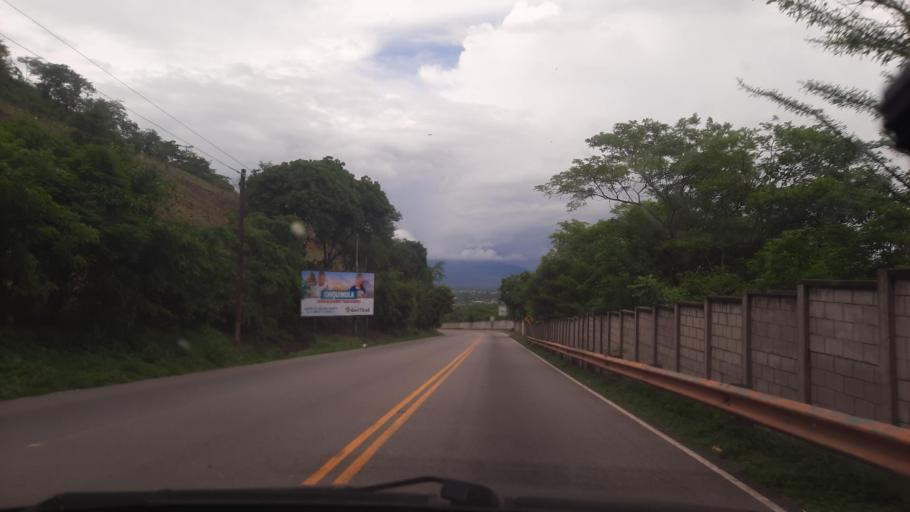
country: GT
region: Chiquimula
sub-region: Municipio de Chiquimula
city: Chiquimula
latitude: 14.8552
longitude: -89.5184
